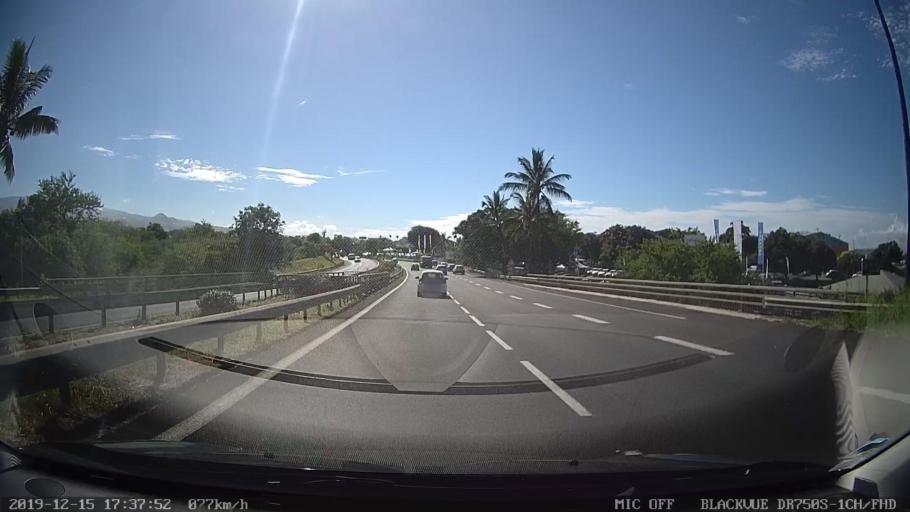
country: RE
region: Reunion
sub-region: Reunion
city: Saint-Pierre
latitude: -21.3325
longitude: 55.4589
